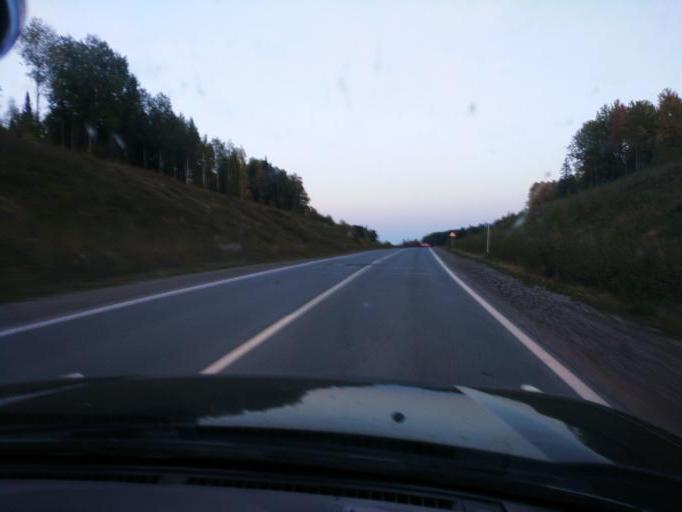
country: RU
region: Perm
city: Sylva
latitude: 58.2947
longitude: 56.8151
